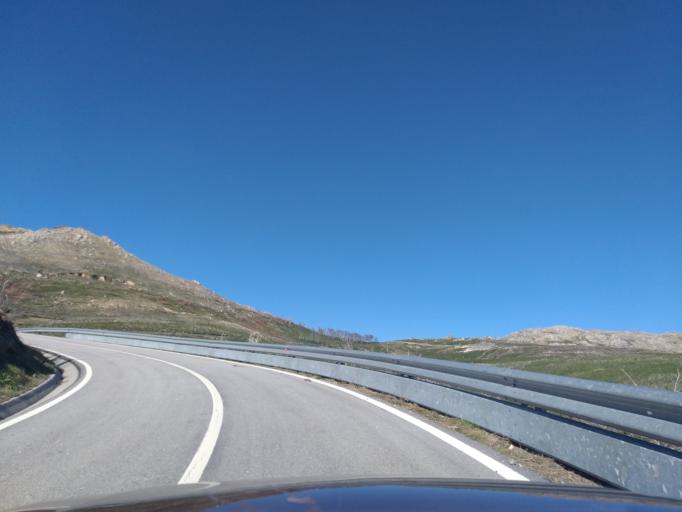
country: PT
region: Guarda
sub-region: Manteigas
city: Manteigas
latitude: 40.4711
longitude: -7.5156
